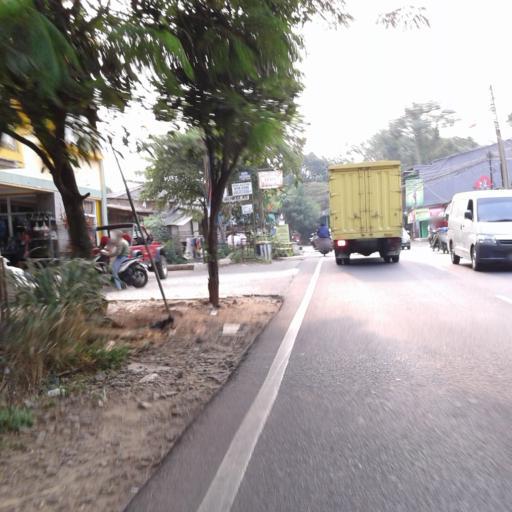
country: ID
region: West Java
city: Sawangan
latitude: -6.4034
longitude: 106.7681
